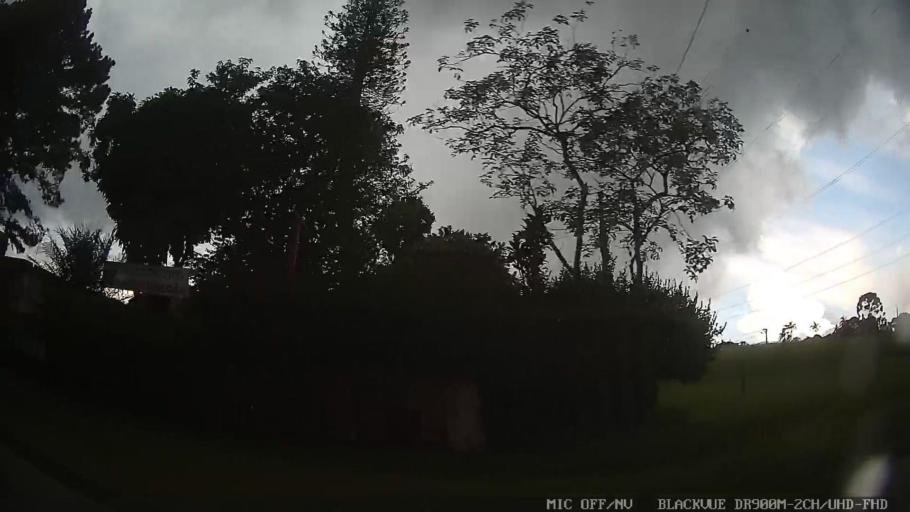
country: BR
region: Sao Paulo
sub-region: Suzano
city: Suzano
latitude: -23.6379
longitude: -46.3168
